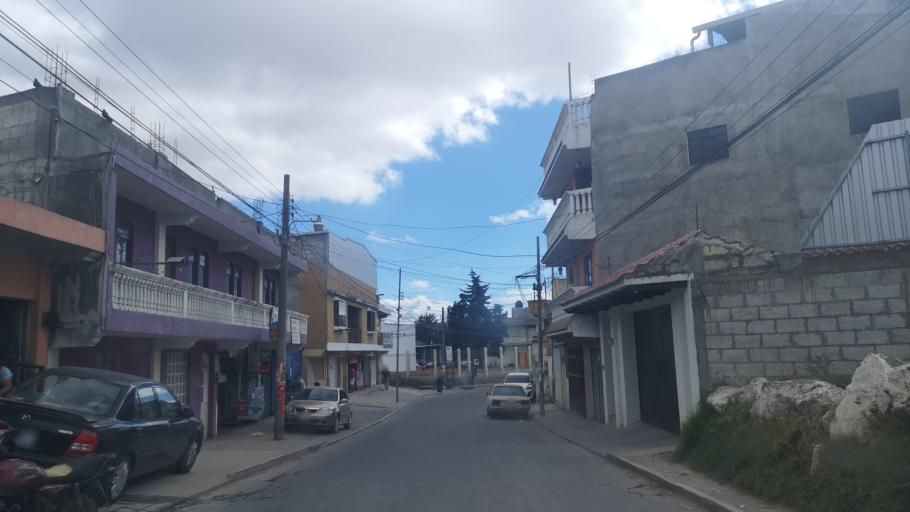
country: GT
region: Quetzaltenango
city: Quetzaltenango
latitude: 14.8373
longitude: -91.5370
